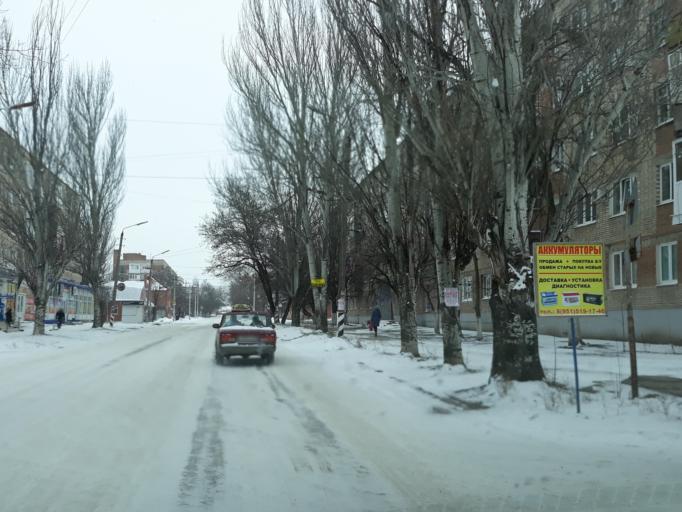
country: RU
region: Rostov
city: Taganrog
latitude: 47.2329
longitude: 38.8790
